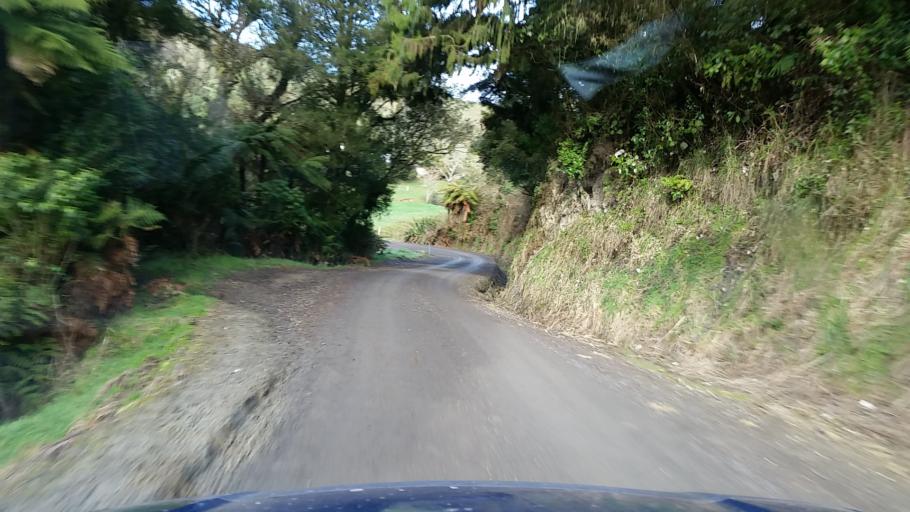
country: NZ
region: Taranaki
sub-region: New Plymouth District
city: Waitara
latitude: -39.0758
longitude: 174.8101
